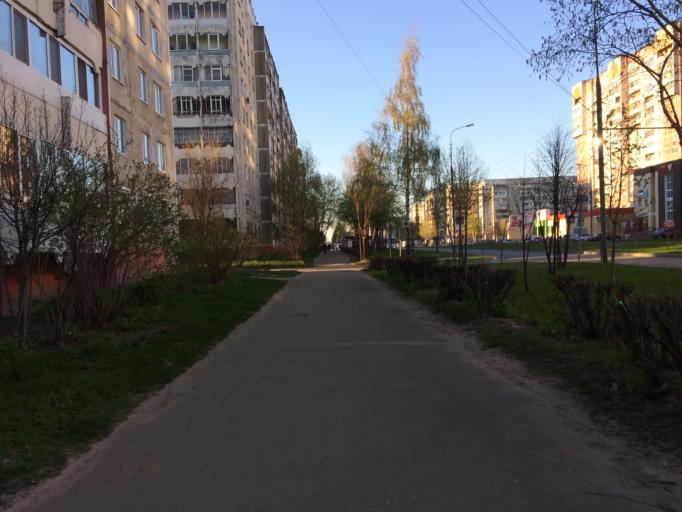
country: RU
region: Mariy-El
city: Yoshkar-Ola
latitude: 56.6287
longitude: 47.9161
